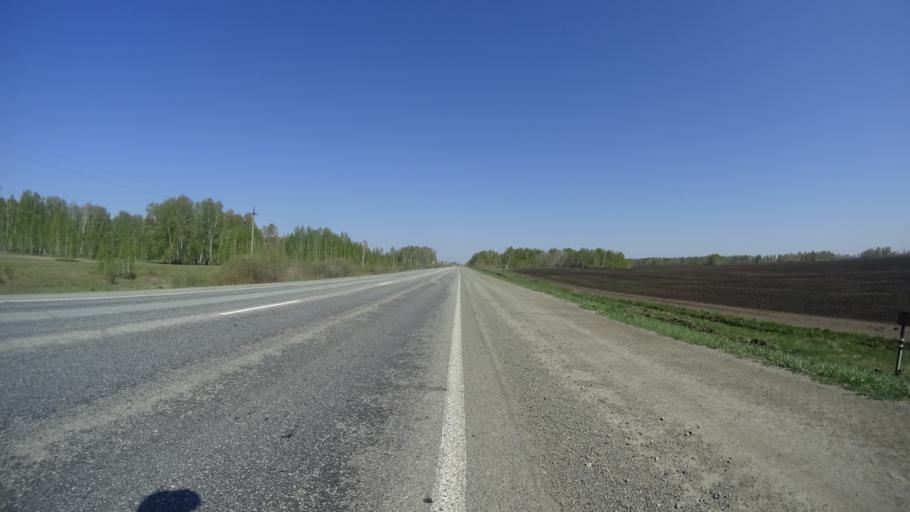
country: RU
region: Chelyabinsk
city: Troitsk
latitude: 54.1801
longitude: 61.4349
